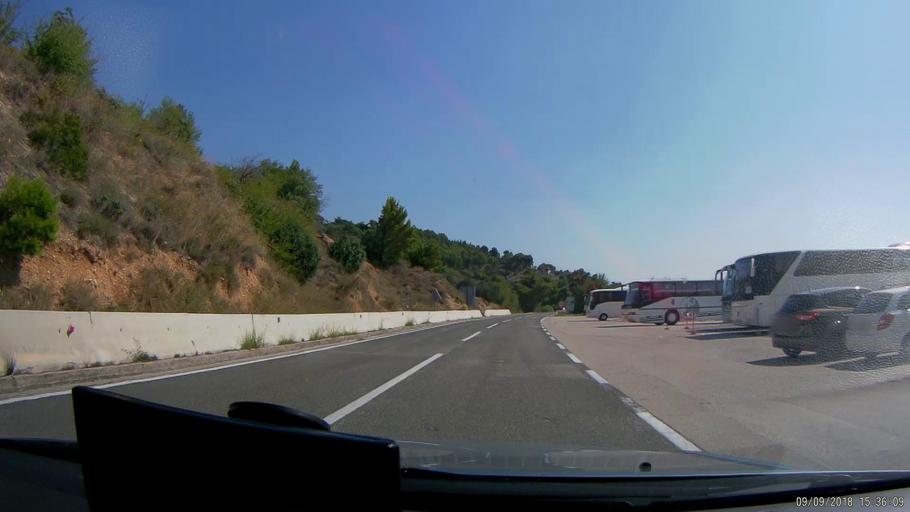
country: HR
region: Splitsko-Dalmatinska
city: Donja Brela
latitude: 43.3804
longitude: 16.9217
